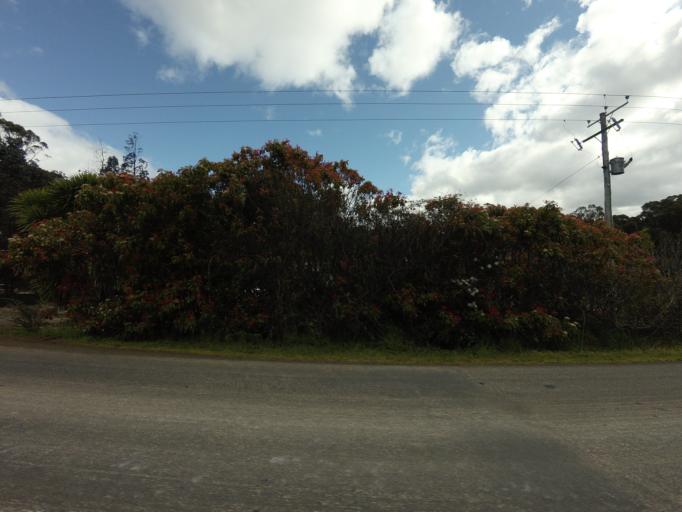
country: AU
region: Tasmania
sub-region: Huon Valley
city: Geeveston
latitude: -43.1900
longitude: 146.9363
